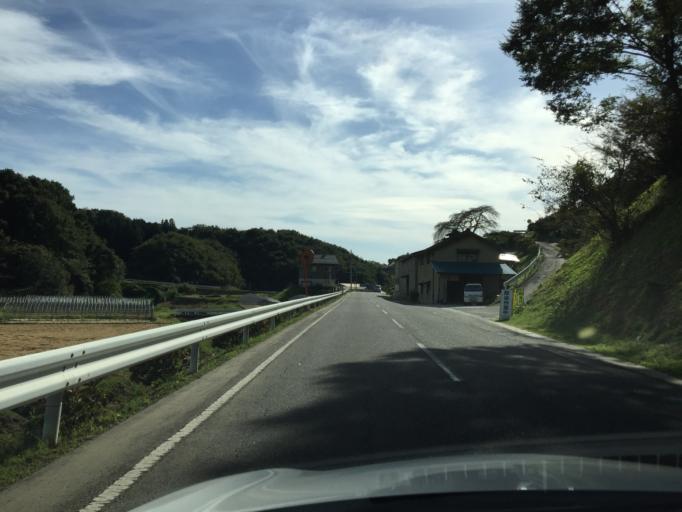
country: JP
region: Fukushima
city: Miharu
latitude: 37.4636
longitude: 140.4940
